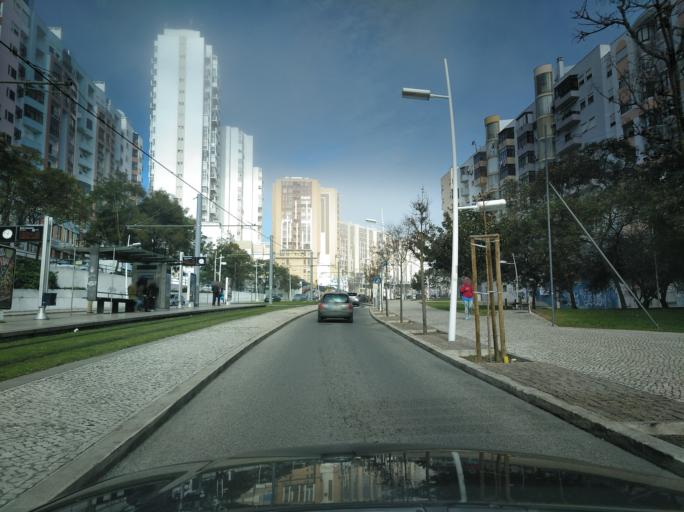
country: PT
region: Setubal
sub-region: Almada
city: Pragal
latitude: 38.6730
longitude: -9.1666
